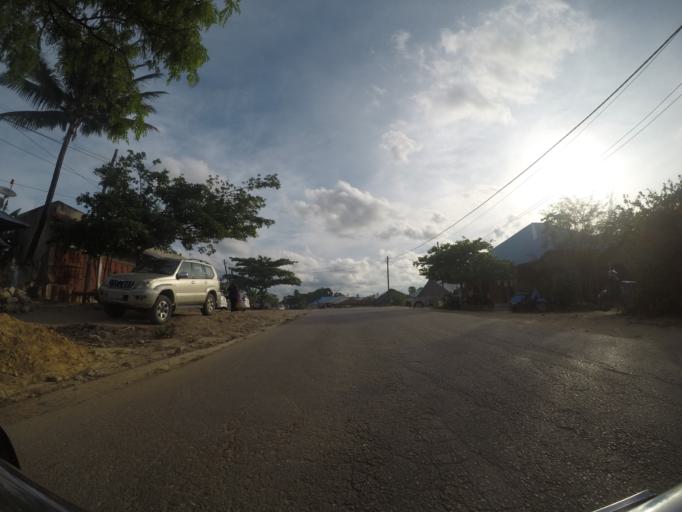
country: TZ
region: Pemba South
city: Chake Chake
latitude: -5.2588
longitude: 39.7745
